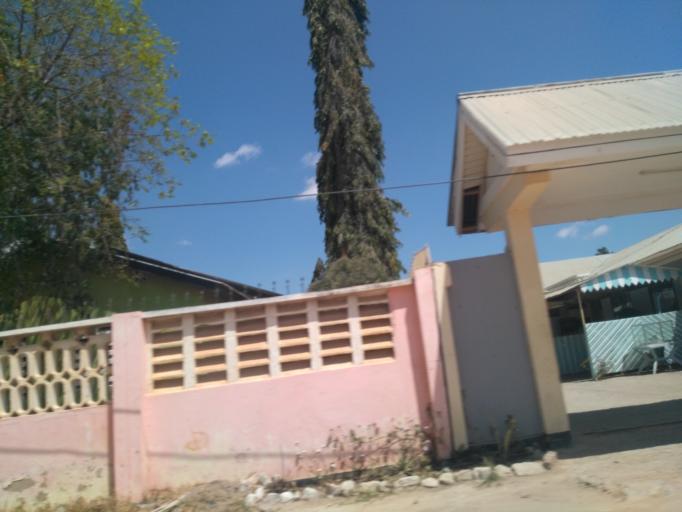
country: TZ
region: Dodoma
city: Dodoma
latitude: -6.1668
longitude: 35.7639
